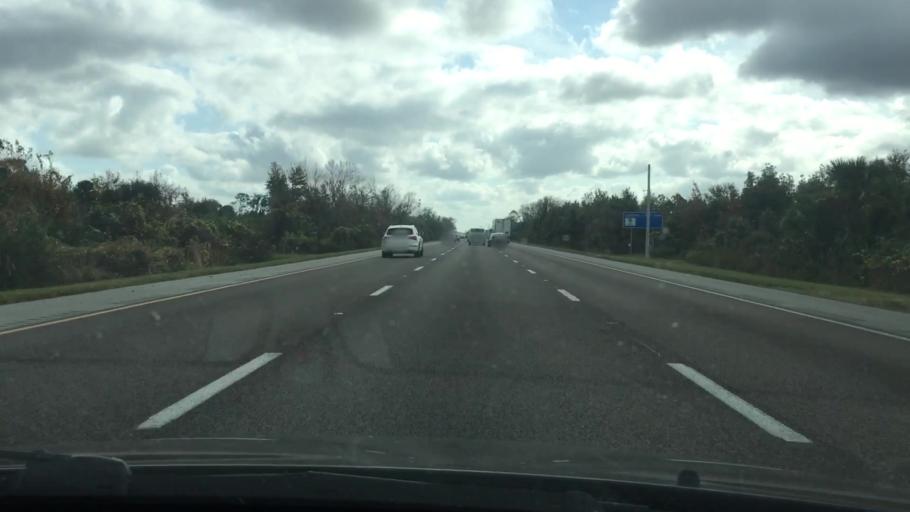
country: US
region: Florida
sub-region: Volusia County
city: Edgewater
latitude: 28.9630
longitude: -80.9568
